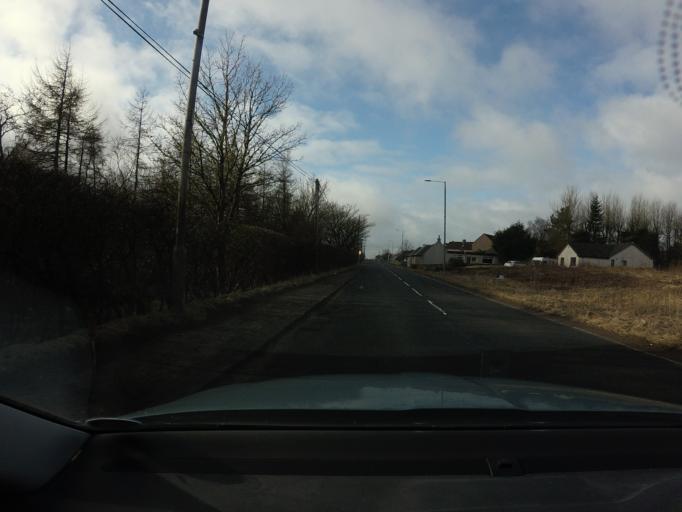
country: GB
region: Scotland
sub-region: South Lanarkshire
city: Forth
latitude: 55.7719
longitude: -3.6827
